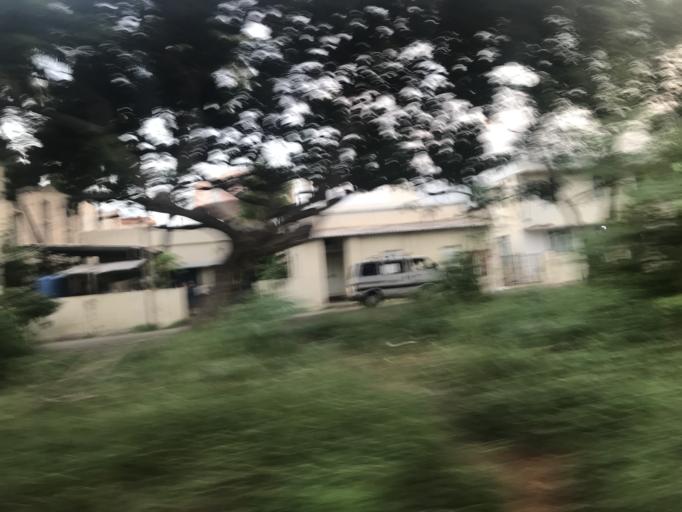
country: IN
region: Tamil Nadu
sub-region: Tiruppur
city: Tiruppur
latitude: 11.1128
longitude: 77.3554
